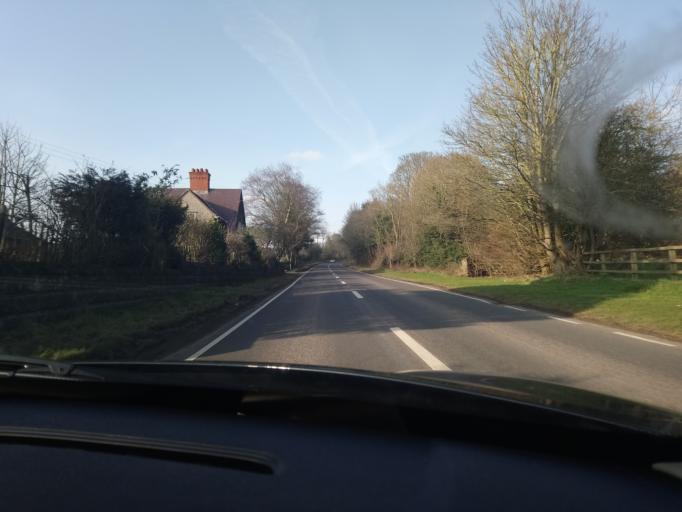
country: GB
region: England
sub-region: Shropshire
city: Clive
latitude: 52.7828
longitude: -2.7544
